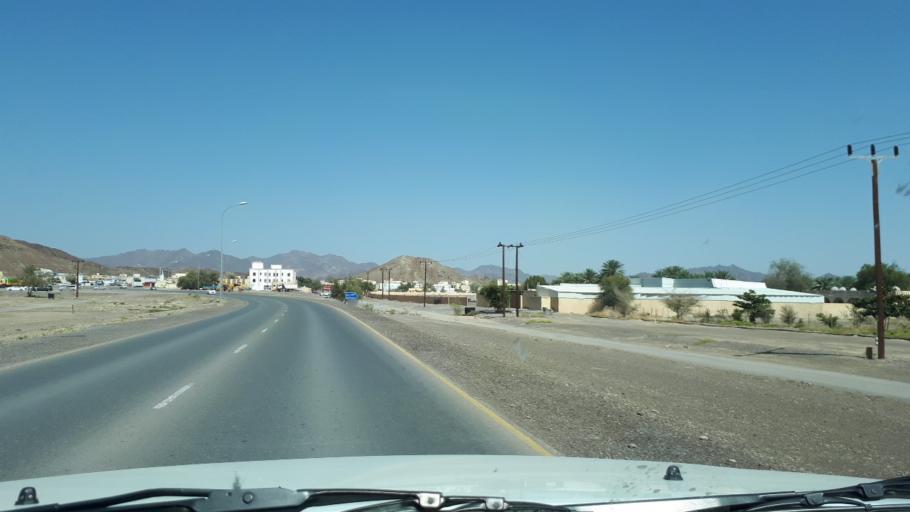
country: OM
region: Muhafazat ad Dakhiliyah
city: Bahla'
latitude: 22.9473
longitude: 57.2804
